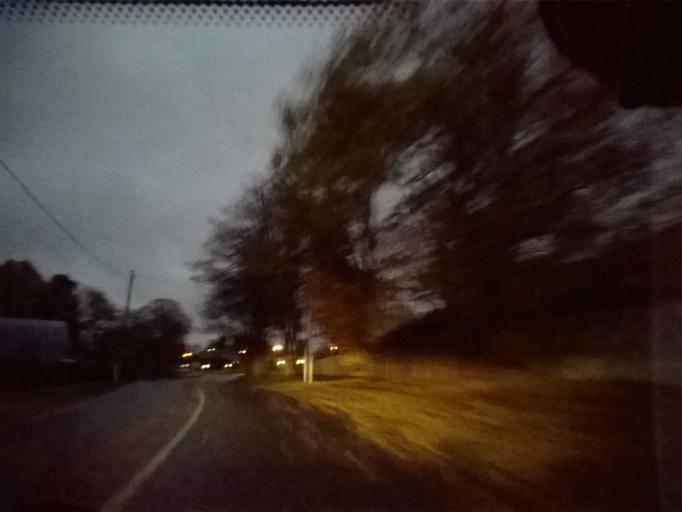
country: EE
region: Harju
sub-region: Viimsi vald
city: Viimsi
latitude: 59.5153
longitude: 24.8484
